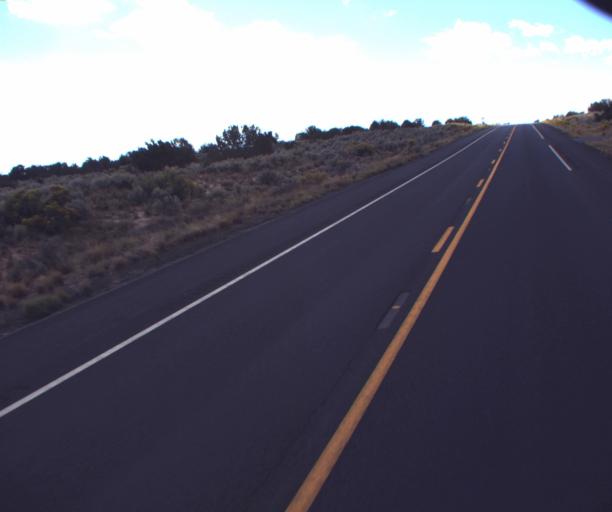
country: US
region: Arizona
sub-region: Apache County
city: Houck
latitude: 35.1897
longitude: -109.3348
